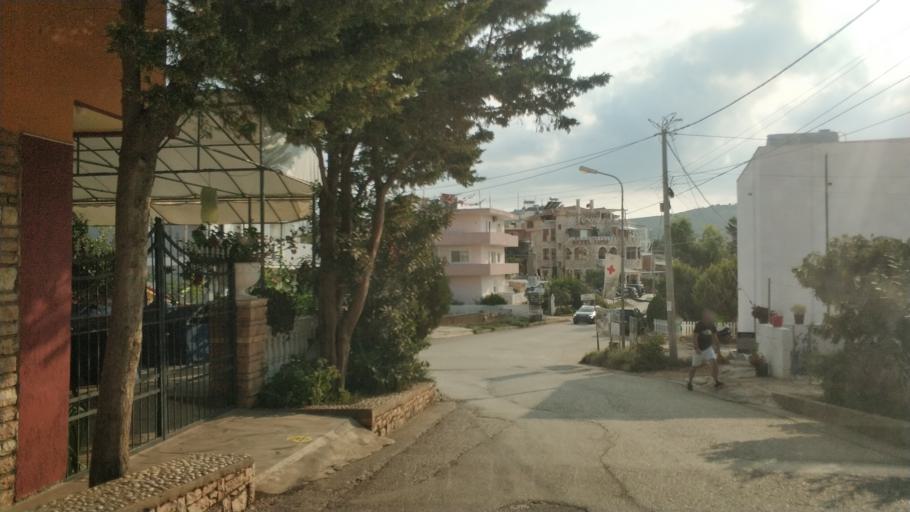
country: AL
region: Vlore
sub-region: Rrethi i Sarandes
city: Xarre
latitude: 39.7683
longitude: 19.9995
